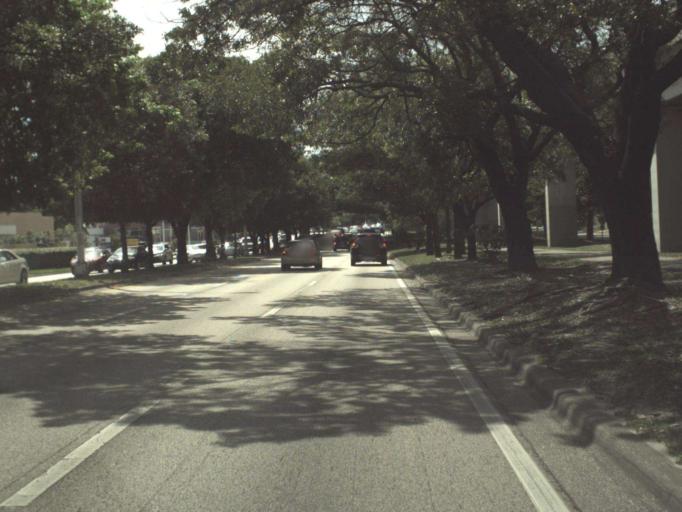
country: US
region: Florida
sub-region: Miami-Dade County
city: Coral Gables
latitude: 25.7364
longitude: -80.2478
